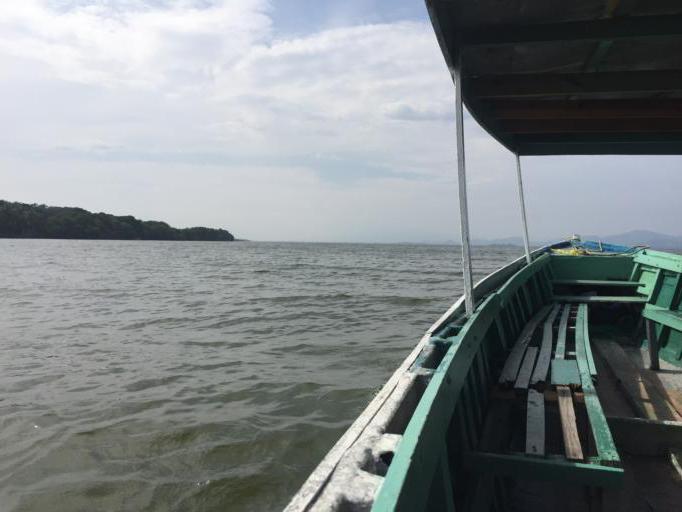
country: MX
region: Guerrero
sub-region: Coyuca de Benitez
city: Colonia Luces en el Mar
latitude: 16.9111
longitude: -99.9764
